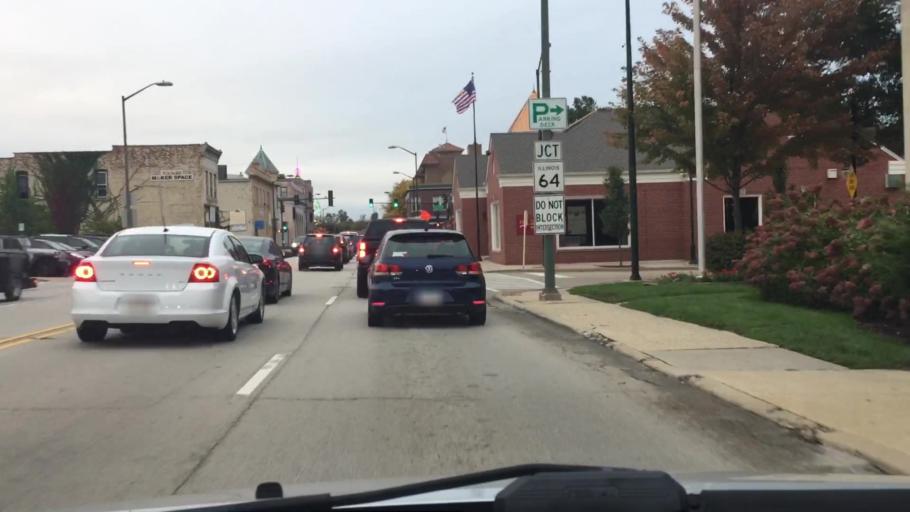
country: US
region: Illinois
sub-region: Kane County
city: Saint Charles
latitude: 41.9122
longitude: -88.3152
